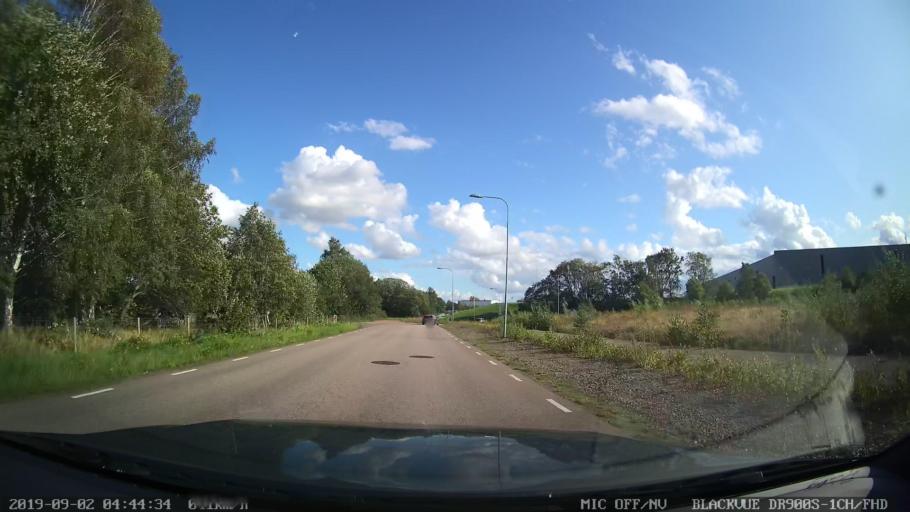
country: SE
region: Skane
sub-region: Helsingborg
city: Odakra
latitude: 56.0764
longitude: 12.7445
